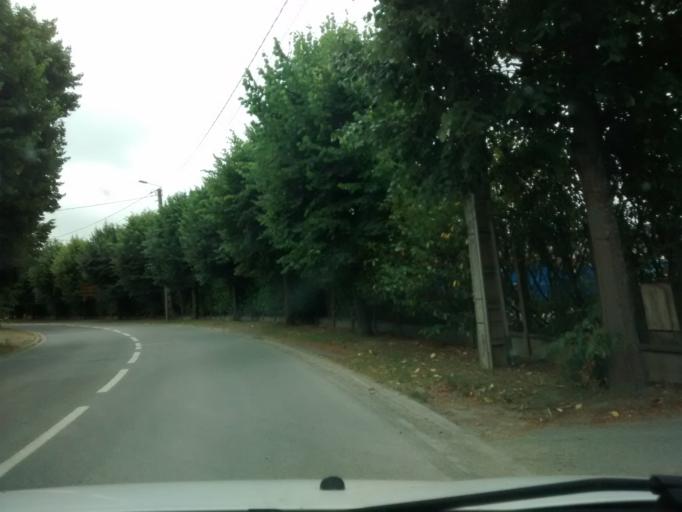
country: FR
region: Brittany
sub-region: Departement d'Ille-et-Vilaine
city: Chantepie
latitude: 48.1030
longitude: -1.6320
